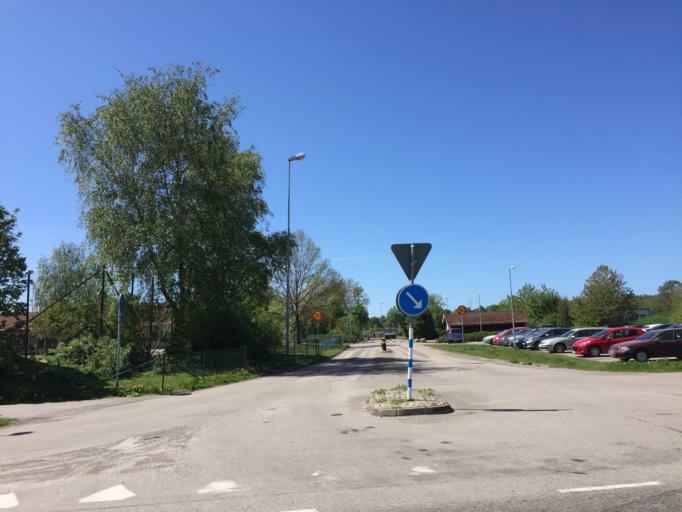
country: SE
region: Halland
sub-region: Varbergs Kommun
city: Varberg
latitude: 57.1159
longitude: 12.2905
